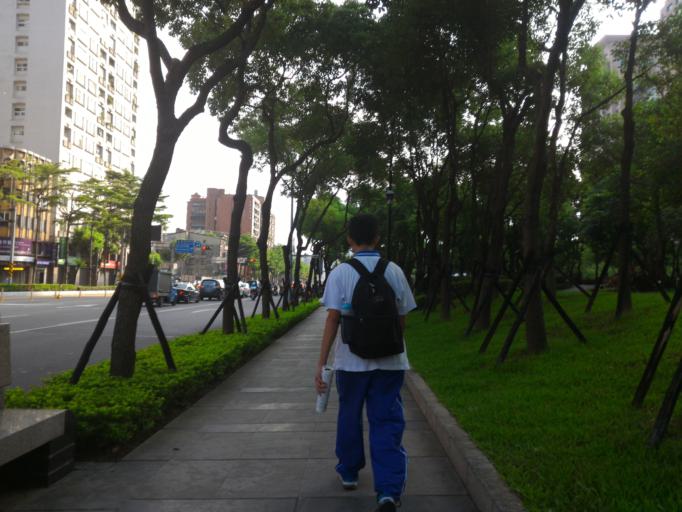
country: TW
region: Taipei
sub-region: Taipei
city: Banqiao
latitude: 25.0133
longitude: 121.4610
